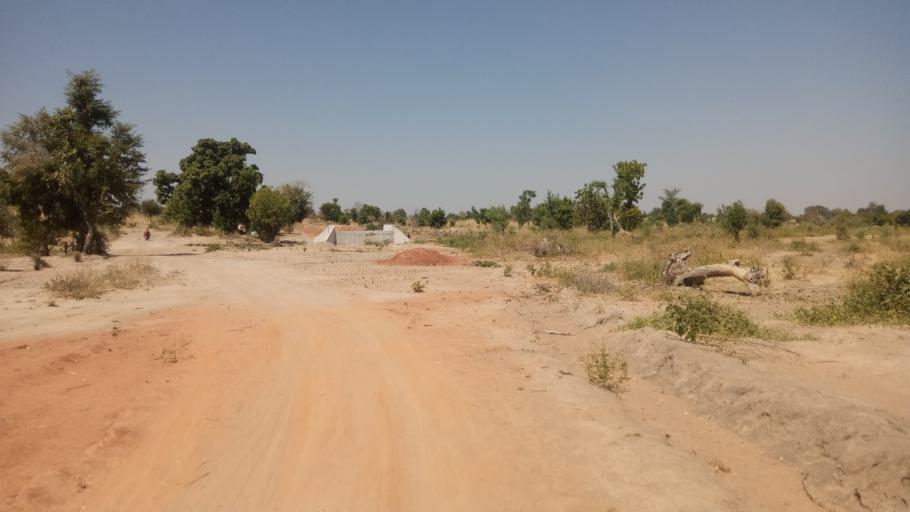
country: NG
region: Adamawa
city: Mayo Belwa
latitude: 9.0921
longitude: 12.0251
